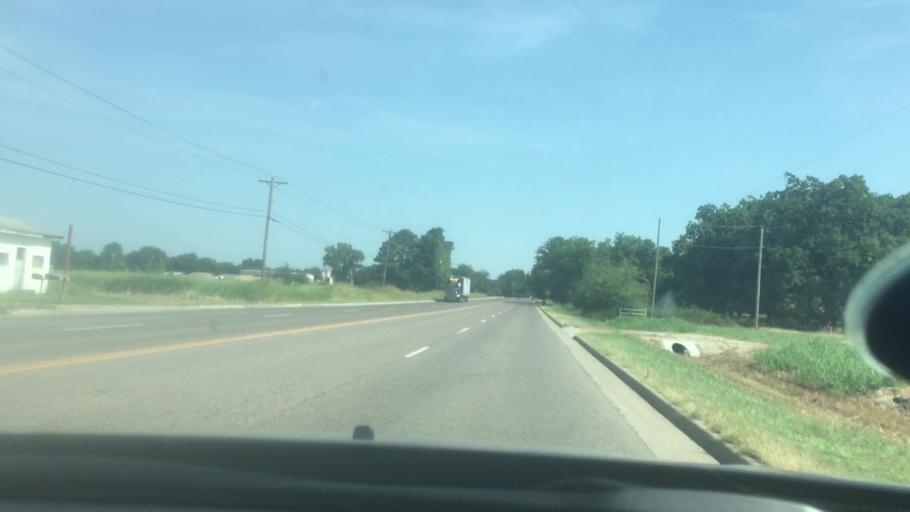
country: US
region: Oklahoma
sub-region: Murray County
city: Davis
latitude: 34.4702
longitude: -97.1313
